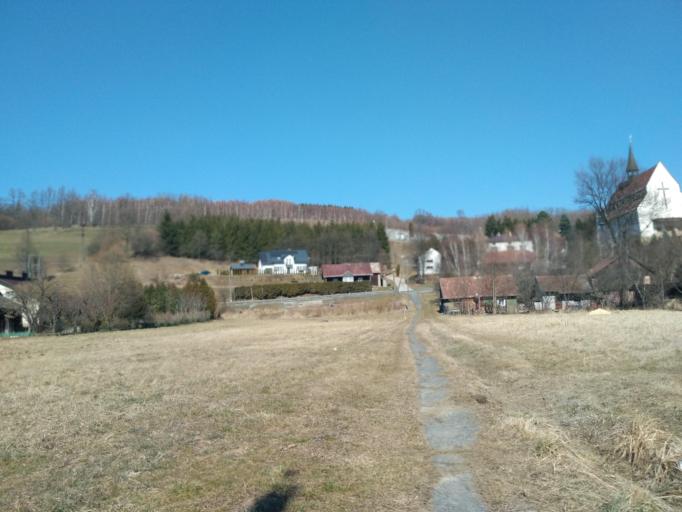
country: PL
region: Subcarpathian Voivodeship
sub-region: Powiat strzyzowski
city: Jawornik
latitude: 49.8039
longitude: 21.8994
